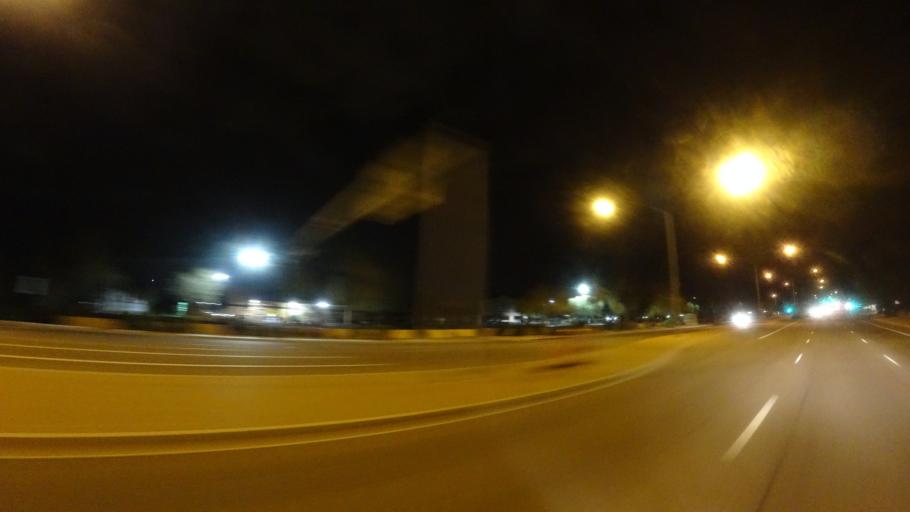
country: US
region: Arizona
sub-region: Maricopa County
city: Gilbert
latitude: 33.3877
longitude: -111.7193
